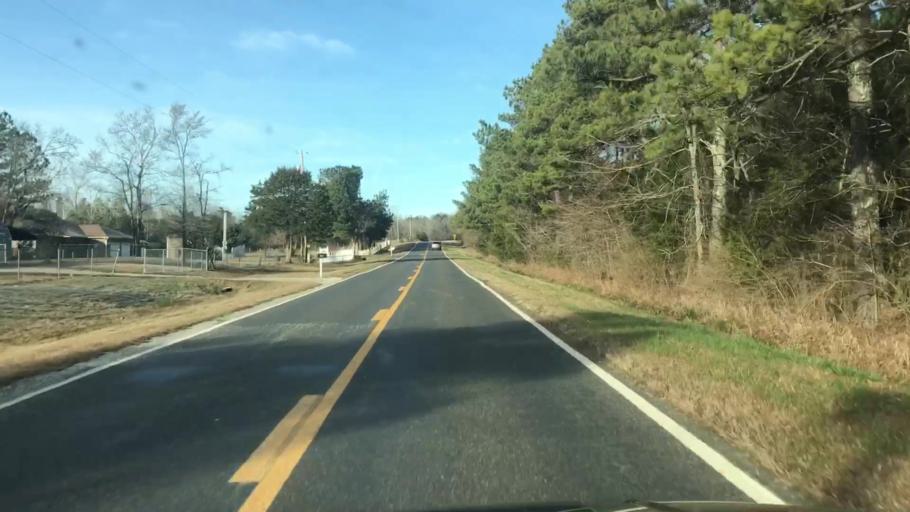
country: US
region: Arkansas
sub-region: Garland County
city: Rockwell
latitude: 34.4712
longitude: -93.2506
